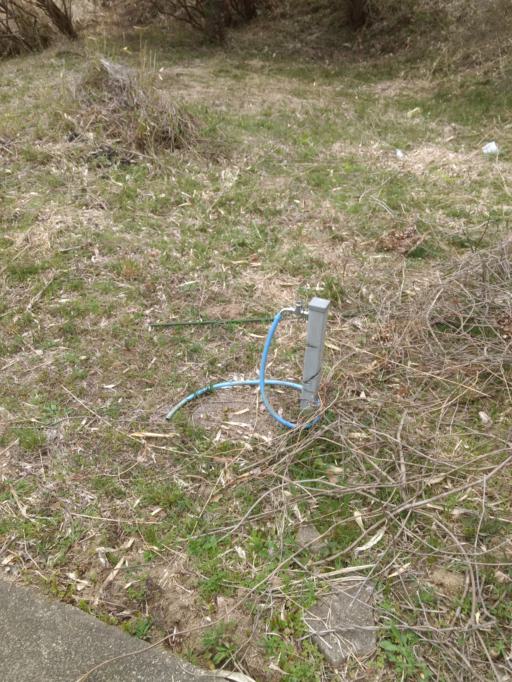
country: JP
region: Kyoto
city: Miyazu
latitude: 35.5555
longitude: 135.2061
